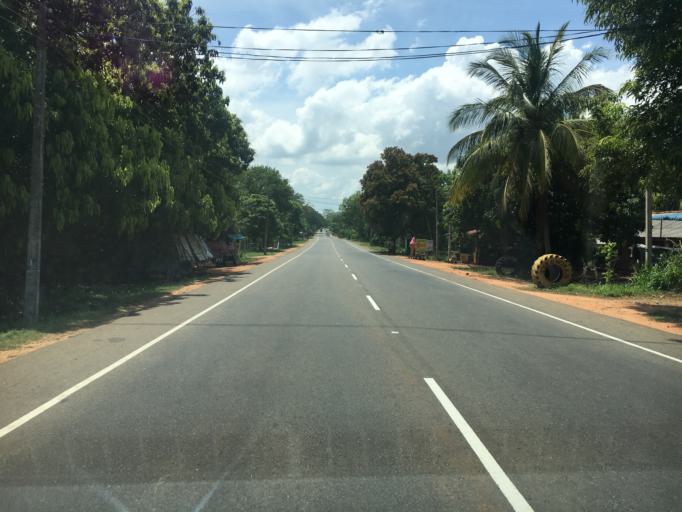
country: LK
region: North Central
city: Anuradhapura
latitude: 8.2644
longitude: 80.5066
